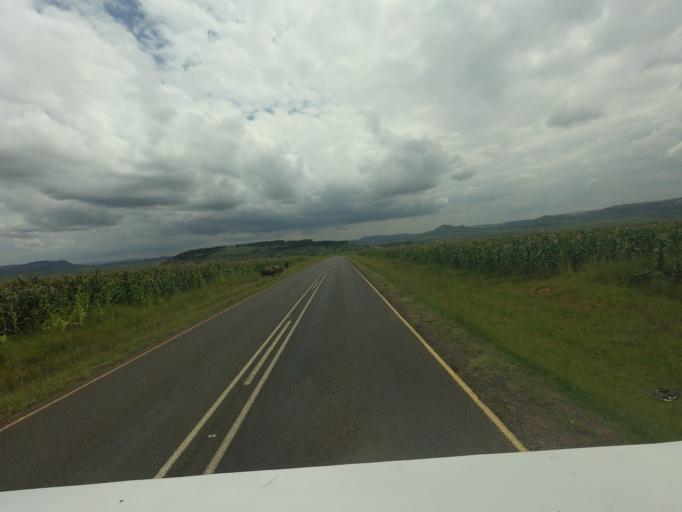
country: LS
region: Leribe
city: Leribe
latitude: -28.9342
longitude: 28.1467
